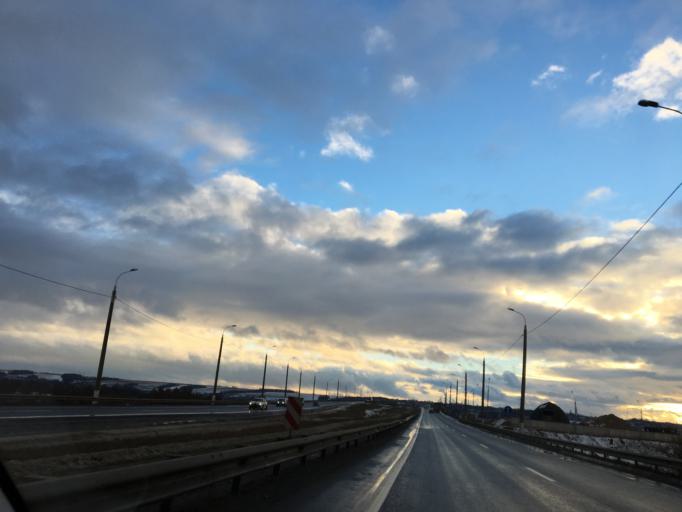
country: RU
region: Moskovskaya
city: Danki
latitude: 54.8747
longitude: 37.5064
